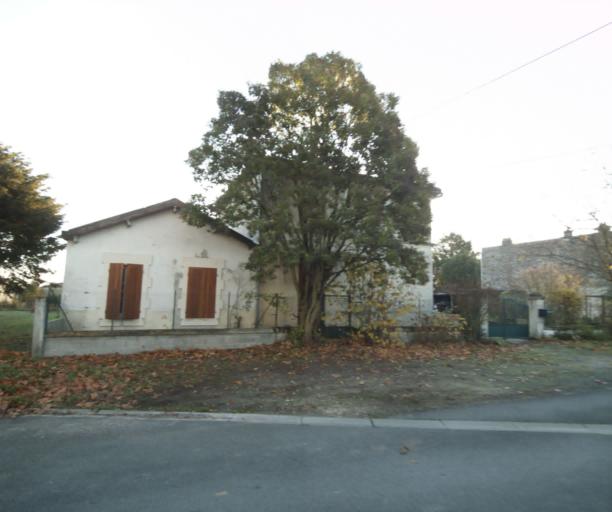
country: FR
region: Poitou-Charentes
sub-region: Departement de la Charente-Maritime
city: Fontcouverte
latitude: 45.7450
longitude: -0.5845
